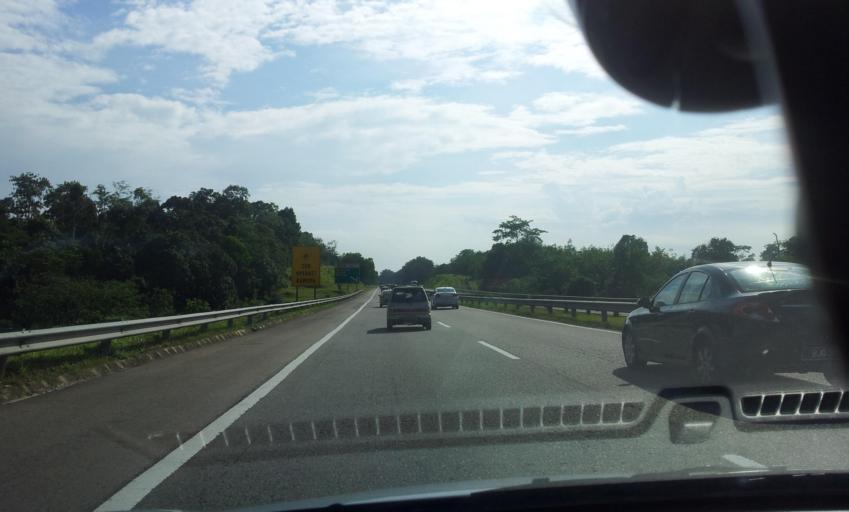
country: MY
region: Pahang
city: Mentekab
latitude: 3.5313
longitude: 102.1920
